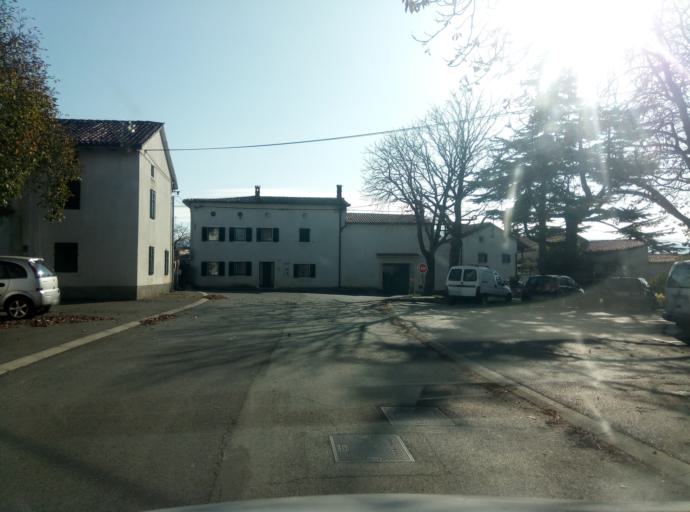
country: SI
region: Komen
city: Komen
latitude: 45.8025
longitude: 13.7123
